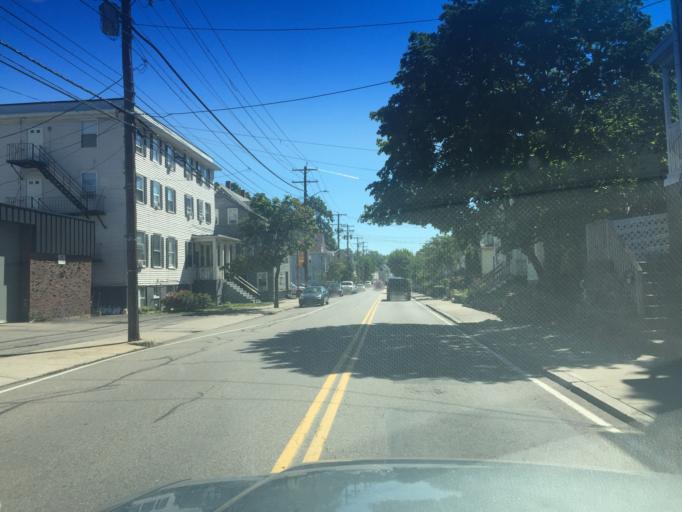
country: US
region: Massachusetts
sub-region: Norfolk County
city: Quincy
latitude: 42.2427
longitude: -71.0182
